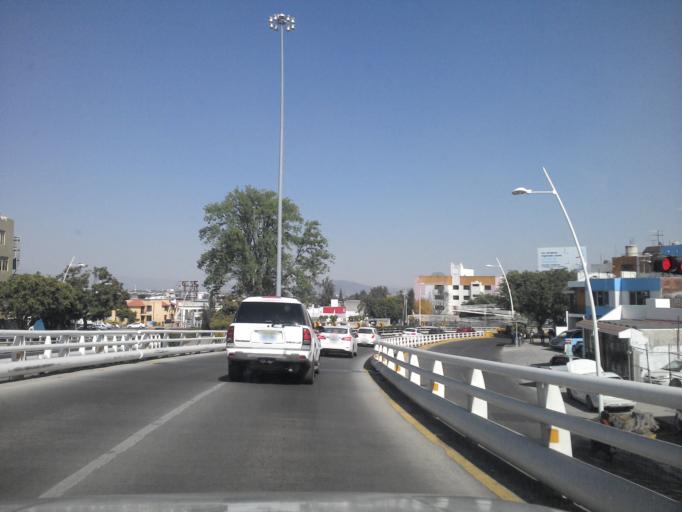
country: MX
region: Jalisco
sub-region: Zapopan
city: Zapopan
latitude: 20.7058
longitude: -103.3636
